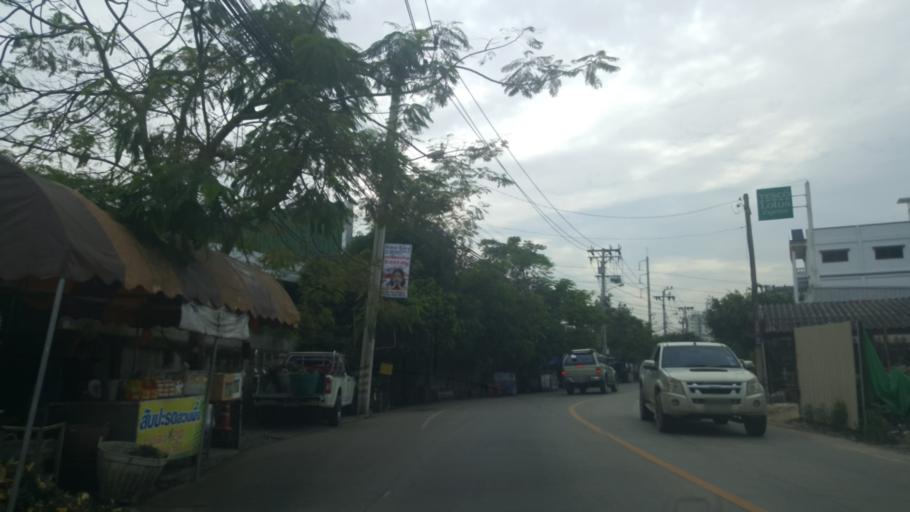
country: TH
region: Bangkok
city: Bang Bon
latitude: 13.6707
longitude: 100.4048
